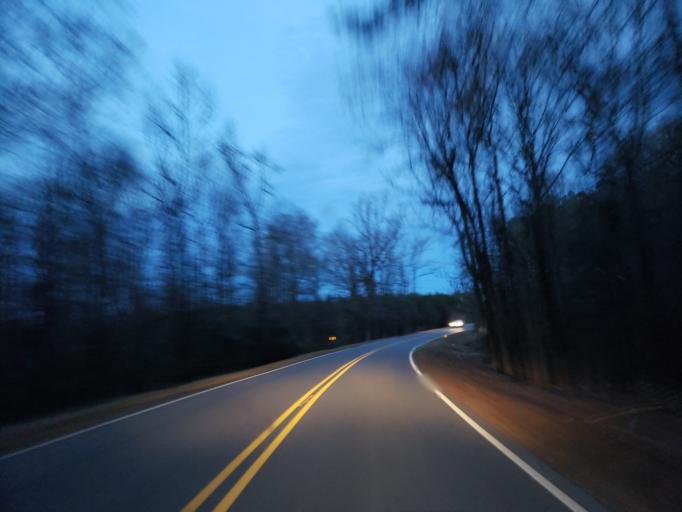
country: US
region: Alabama
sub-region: Greene County
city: Eutaw
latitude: 32.9028
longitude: -88.0263
